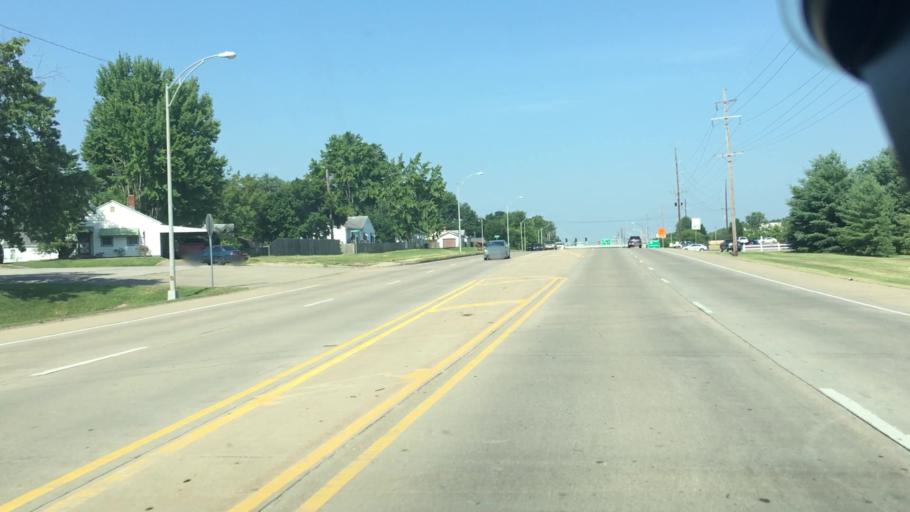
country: US
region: Indiana
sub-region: Vanderburgh County
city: Melody Hill
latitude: 37.9991
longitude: -87.5321
